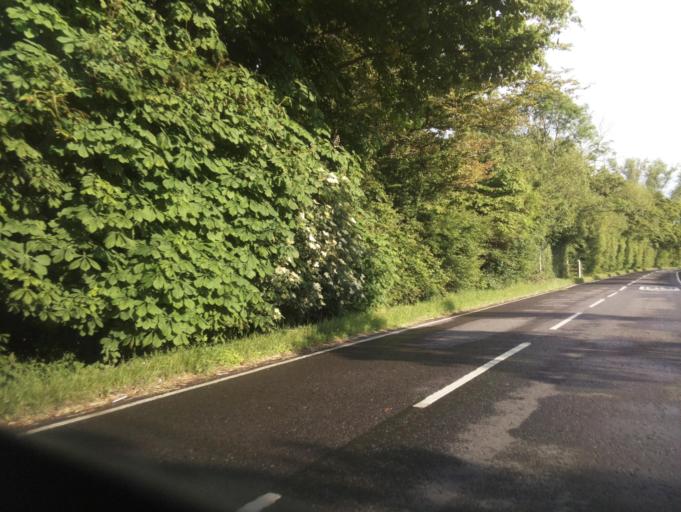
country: GB
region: England
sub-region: Lincolnshire
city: Navenby
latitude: 53.0587
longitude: -0.6411
